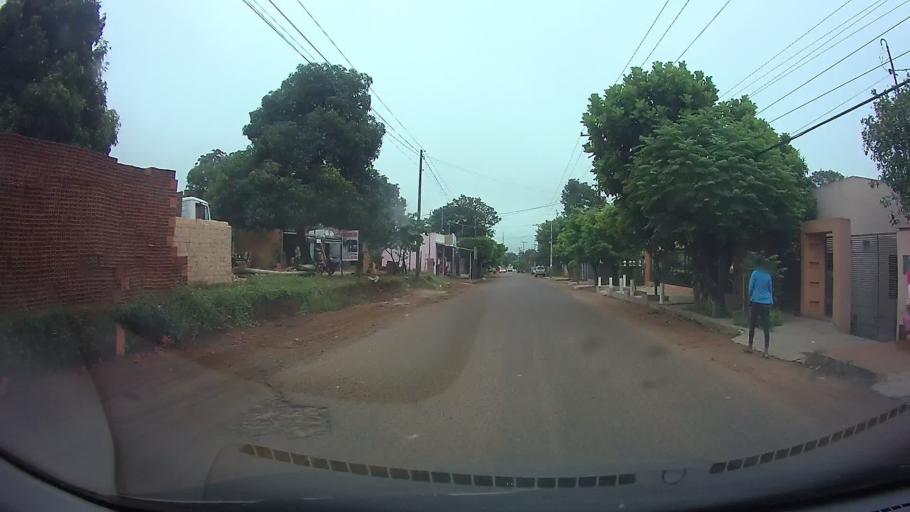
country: PY
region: Central
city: Itaugua
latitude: -25.3877
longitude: -57.3513
